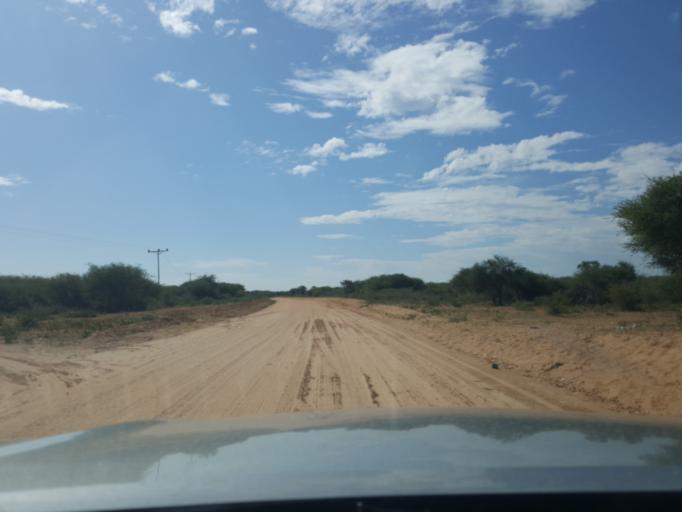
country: BW
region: Kweneng
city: Khudumelapye
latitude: -23.8138
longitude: 24.8219
